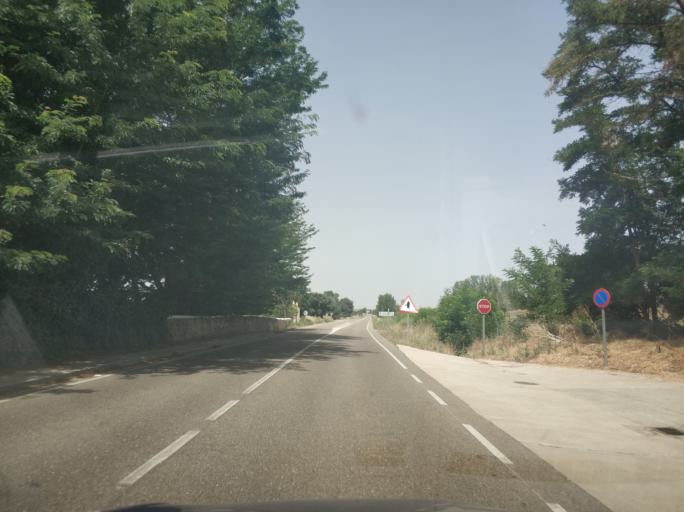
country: ES
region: Castille and Leon
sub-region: Provincia de Salamanca
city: Valverdon
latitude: 41.0418
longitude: -5.7569
